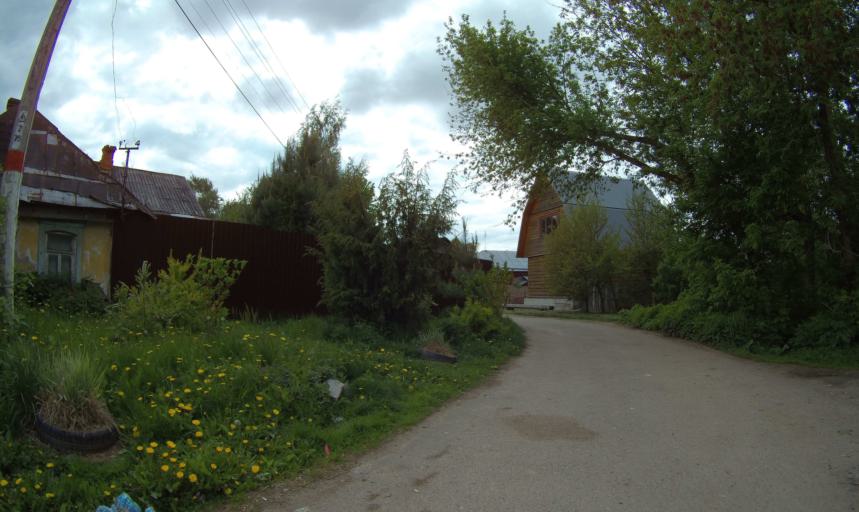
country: RU
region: Moskovskaya
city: Raduzhnyy
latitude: 55.1014
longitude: 38.7446
